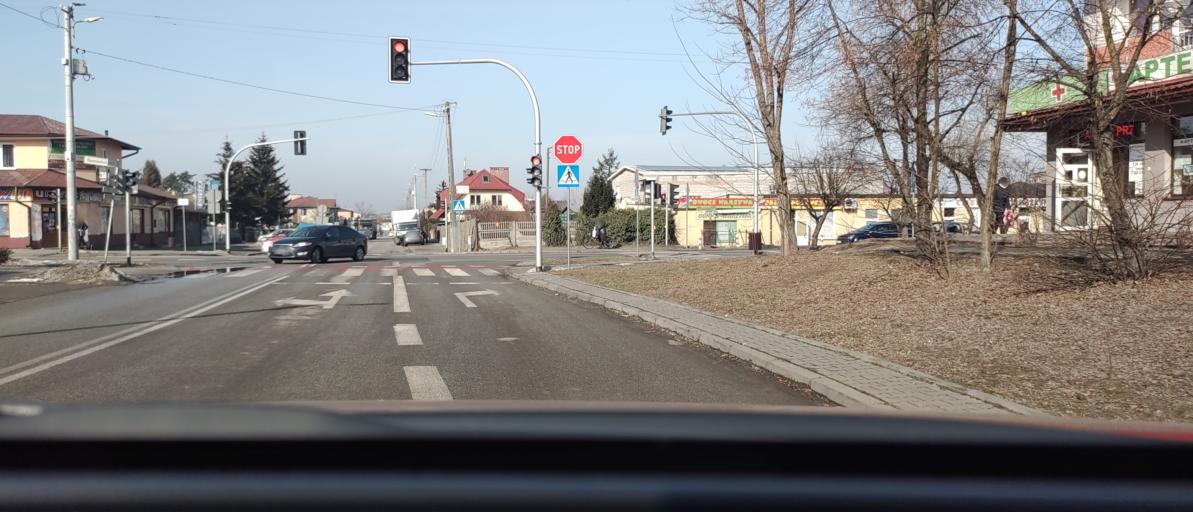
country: PL
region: Masovian Voivodeship
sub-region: Powiat bialobrzeski
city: Bialobrzegi
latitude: 51.6439
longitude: 20.9509
